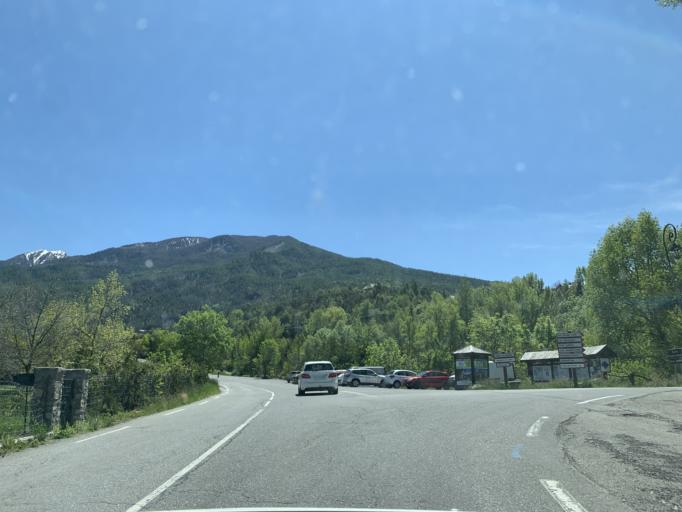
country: FR
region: Provence-Alpes-Cote d'Azur
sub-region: Departement des Hautes-Alpes
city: Embrun
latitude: 44.5385
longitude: 6.4973
